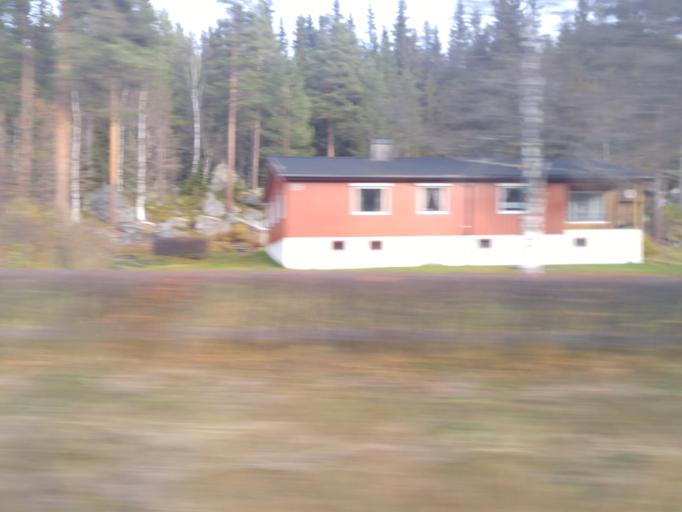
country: NO
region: Oppland
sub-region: Nord-Aurdal
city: Fagernes
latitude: 61.0380
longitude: 9.1751
